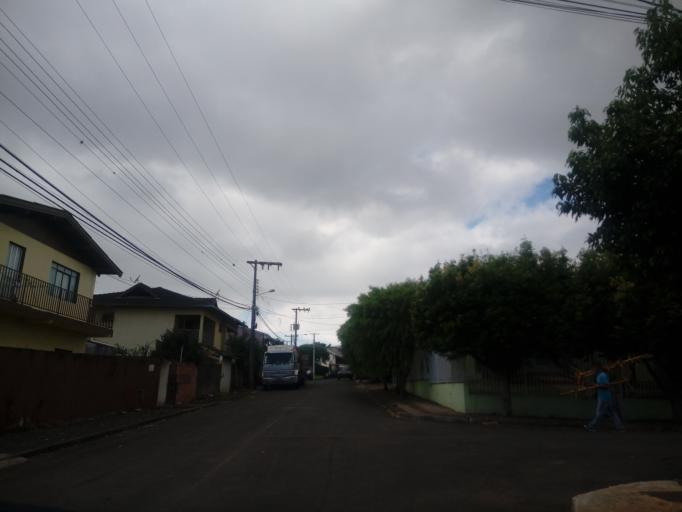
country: BR
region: Santa Catarina
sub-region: Chapeco
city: Chapeco
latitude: -27.1153
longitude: -52.6248
